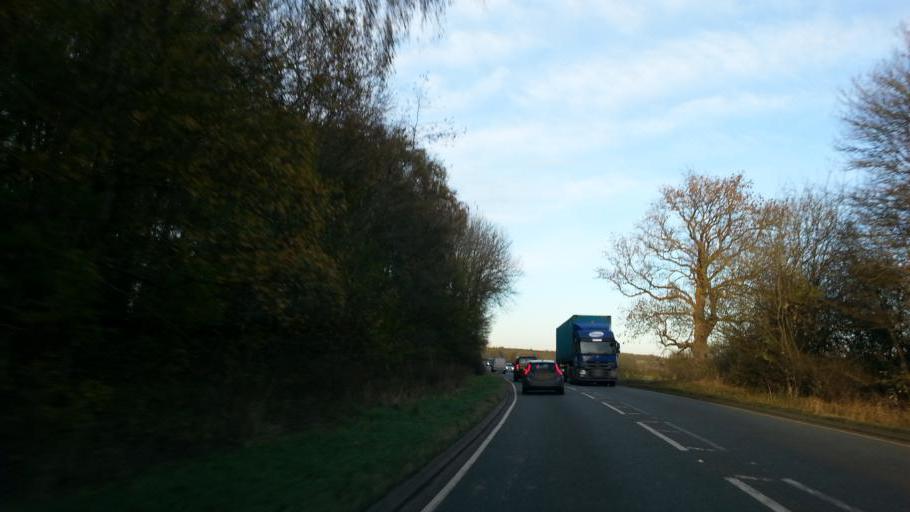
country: GB
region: England
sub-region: Northamptonshire
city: Corby
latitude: 52.5116
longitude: -0.6016
